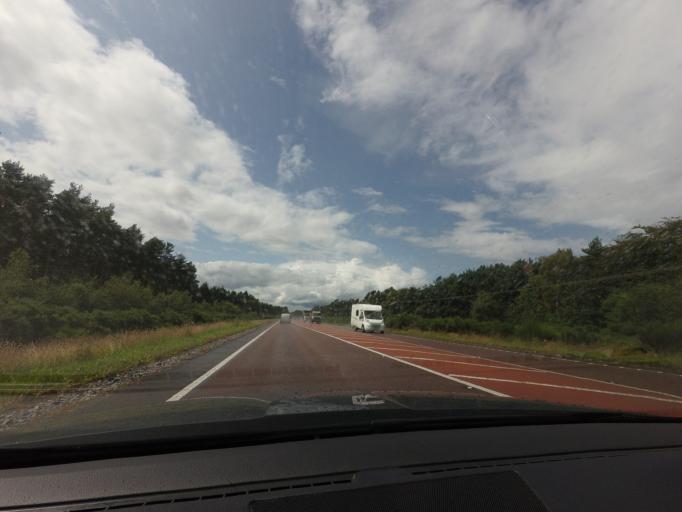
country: GB
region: Scotland
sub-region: Moray
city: Fochabers
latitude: 57.6230
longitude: -3.1285
